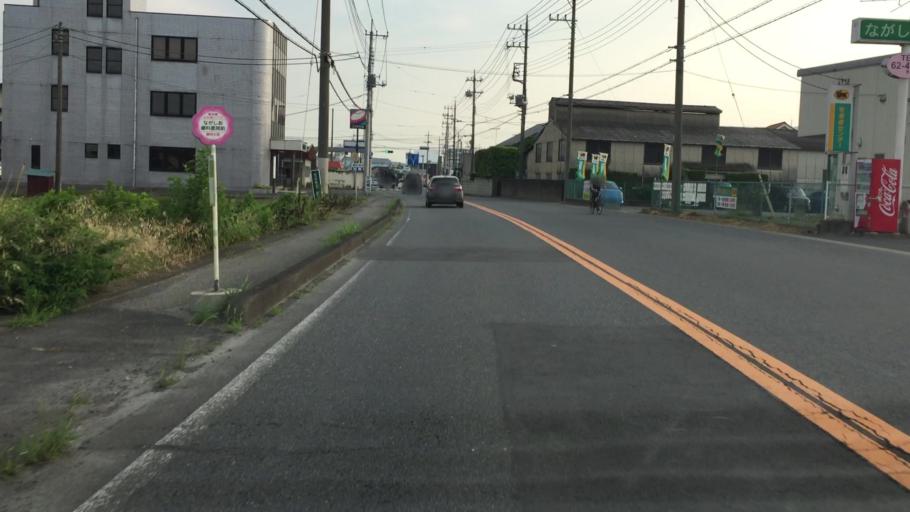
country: JP
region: Tochigi
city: Fujioka
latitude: 36.2772
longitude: 139.6578
